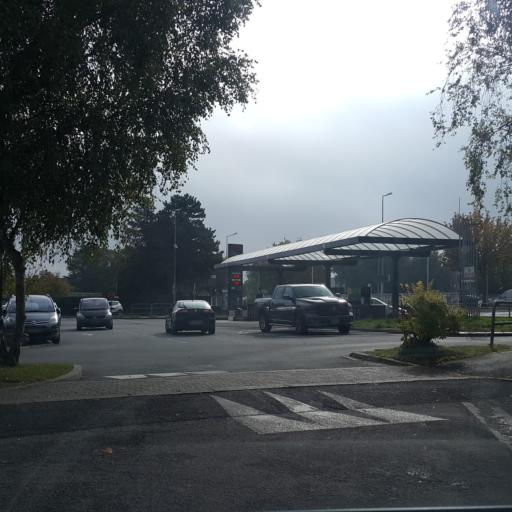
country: FR
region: Ile-de-France
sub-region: Departement de l'Essonne
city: Saint-Germain-les-Corbeil
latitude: 48.6199
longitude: 2.4923
